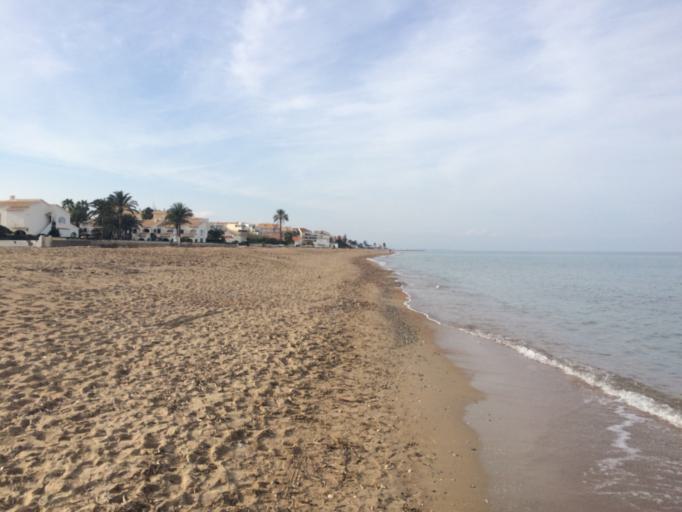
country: ES
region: Valencia
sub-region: Provincia de Alicante
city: els Poblets
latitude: 38.8606
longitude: 0.0331
